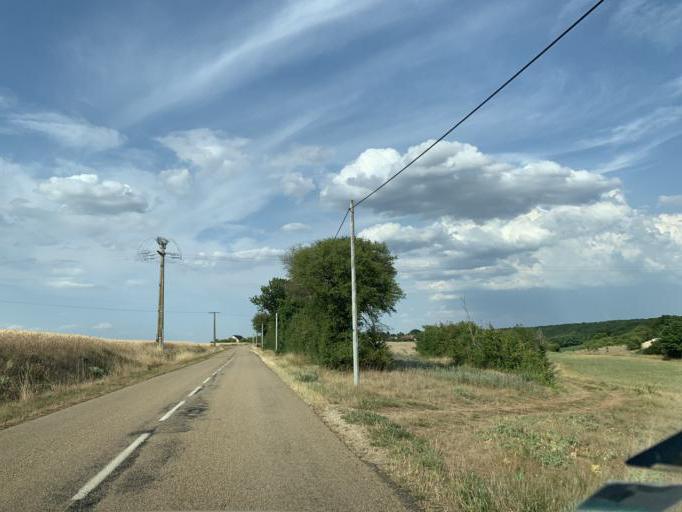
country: FR
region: Bourgogne
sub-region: Departement de l'Yonne
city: Fontenailles
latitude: 47.5192
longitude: 3.3759
